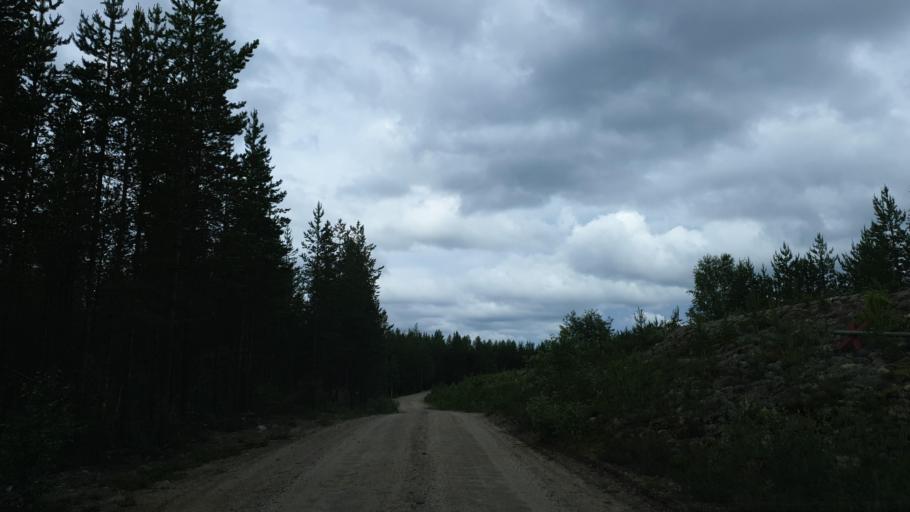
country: SE
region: Jaemtland
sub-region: Harjedalens Kommun
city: Sveg
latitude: 62.0426
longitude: 14.4902
